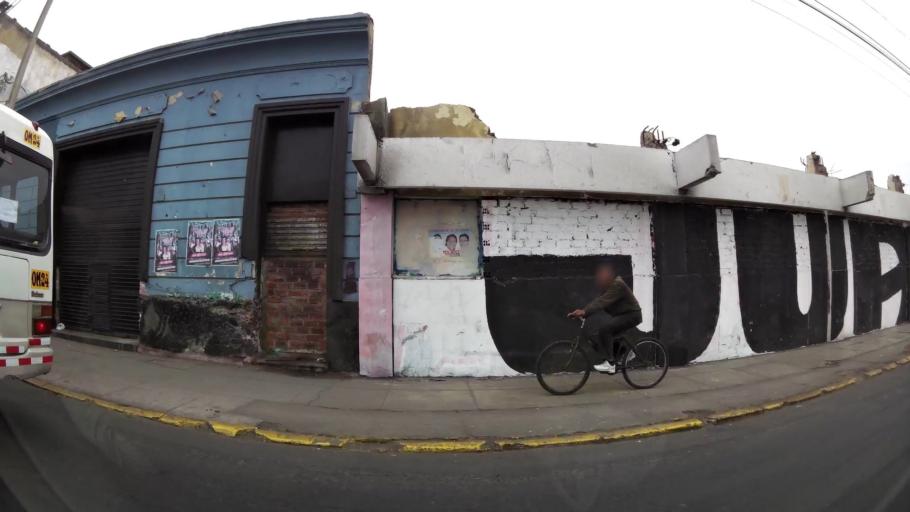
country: PE
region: Callao
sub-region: Callao
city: Callao
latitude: -12.0621
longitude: -77.1469
